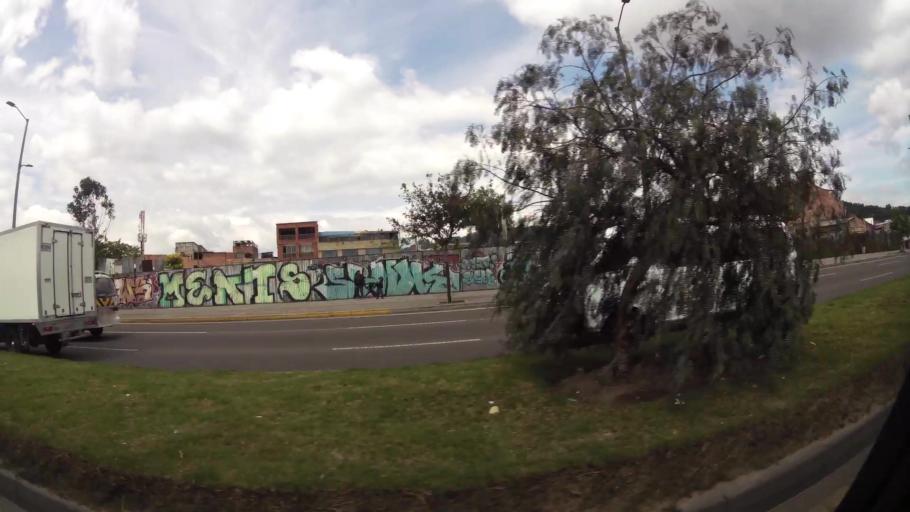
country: CO
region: Bogota D.C.
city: Barrio San Luis
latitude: 4.7191
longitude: -74.0941
